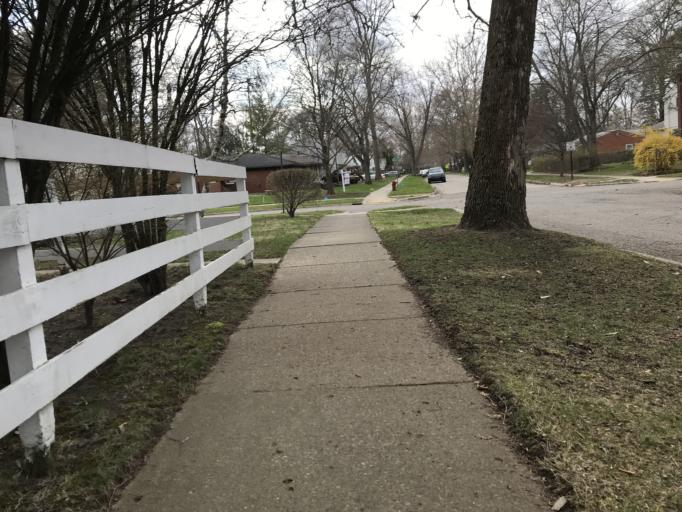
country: US
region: Michigan
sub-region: Oakland County
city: Farmington
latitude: 42.4664
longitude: -83.3427
